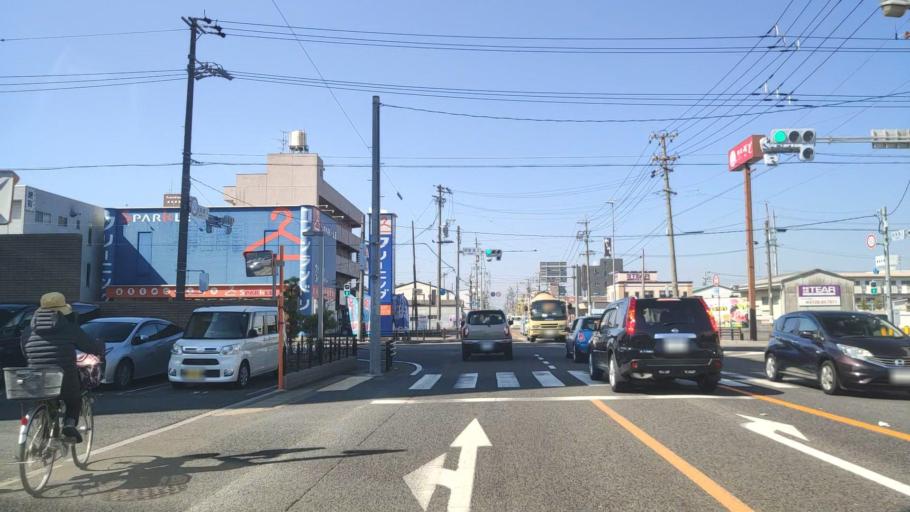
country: JP
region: Gifu
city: Gifu-shi
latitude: 35.3974
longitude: 136.7658
